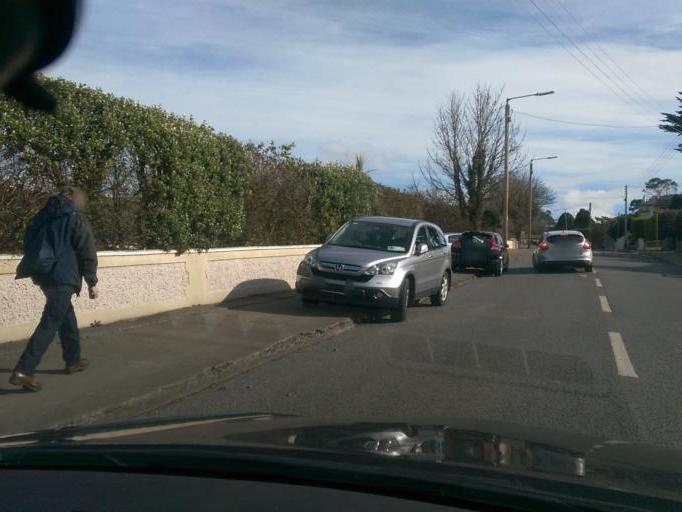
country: IE
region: Leinster
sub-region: Fingal County
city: Howth
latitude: 53.3826
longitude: -6.0601
